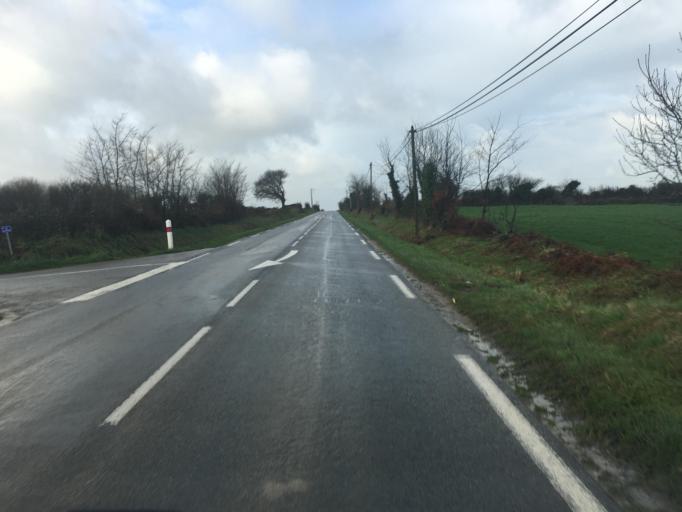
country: FR
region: Lower Normandy
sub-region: Departement de la Manche
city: Saint-Pierre-Eglise
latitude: 49.6705
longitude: -1.3461
